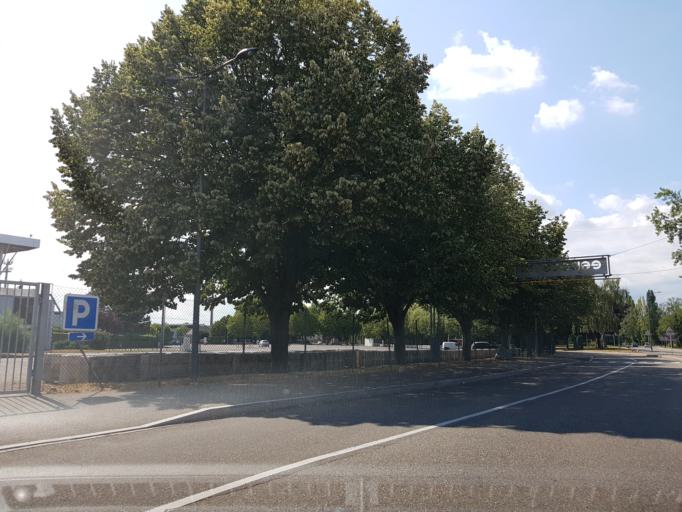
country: FR
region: Alsace
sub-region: Departement du Haut-Rhin
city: Illzach
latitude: 47.7776
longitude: 7.3534
